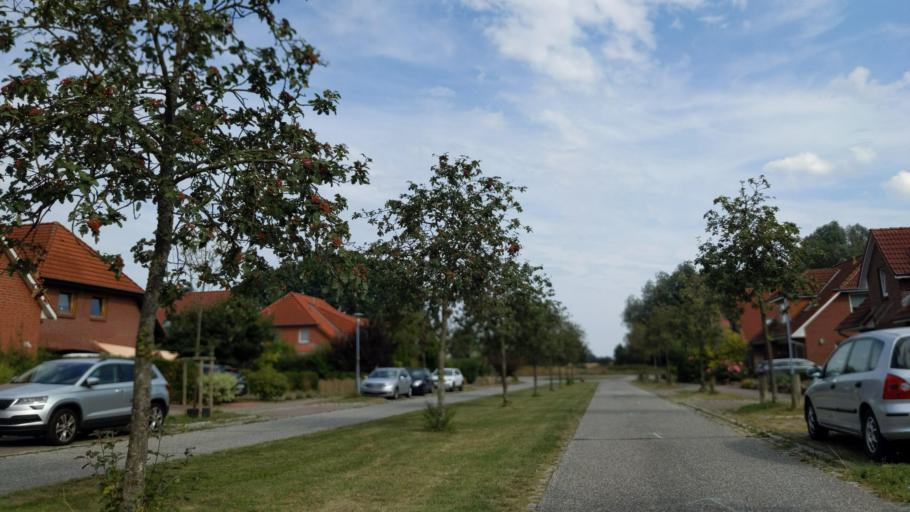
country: DE
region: Schleswig-Holstein
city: Gross Gronau
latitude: 53.8452
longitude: 10.7639
